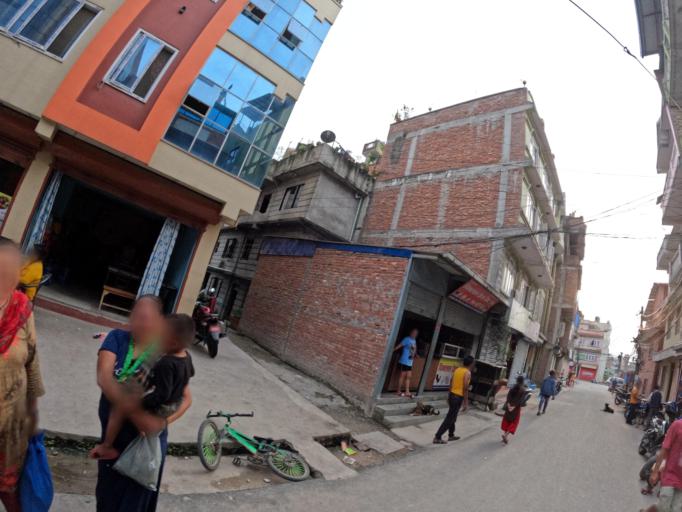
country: NP
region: Central Region
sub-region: Bagmati Zone
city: Bhaktapur
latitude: 27.6836
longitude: 85.3902
